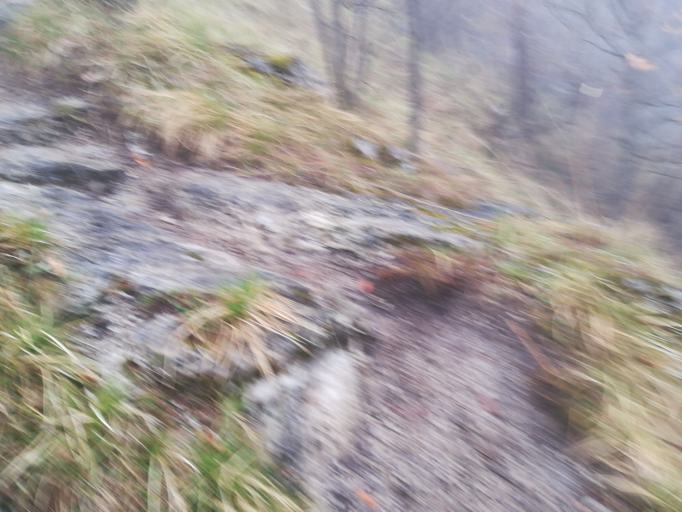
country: HR
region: Varazdinska
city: Ivanec
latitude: 46.1885
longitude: 16.1391
